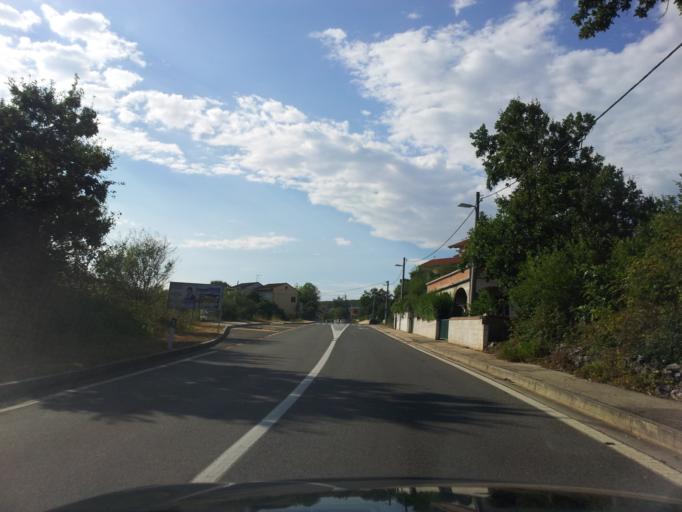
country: HR
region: Zadarska
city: Posedarje
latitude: 44.2149
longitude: 15.4685
